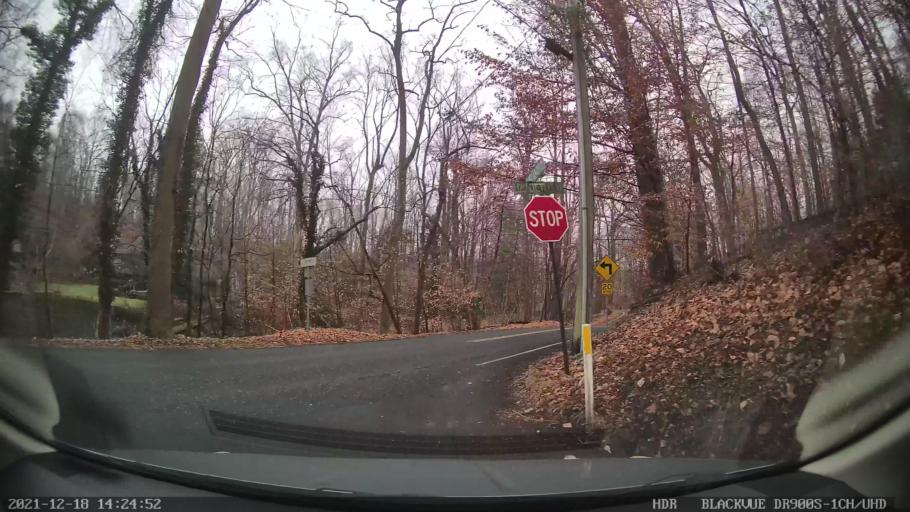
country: US
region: Pennsylvania
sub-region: Berks County
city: Oley
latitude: 40.4171
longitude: -75.7455
